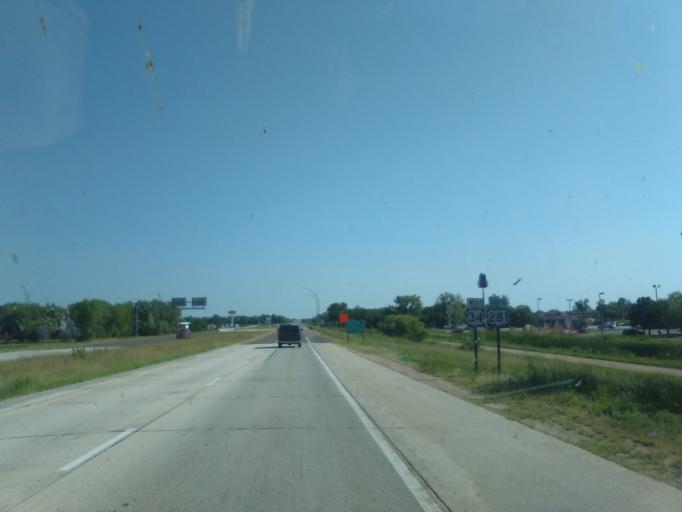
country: US
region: Nebraska
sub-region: Hall County
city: Grand Island
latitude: 40.8177
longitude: -98.3786
